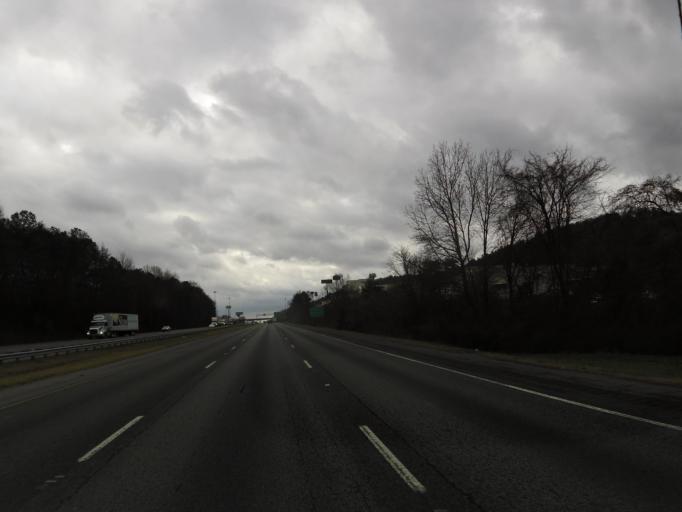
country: US
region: Georgia
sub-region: Whitfield County
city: Dalton
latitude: 34.7680
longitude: -85.0016
